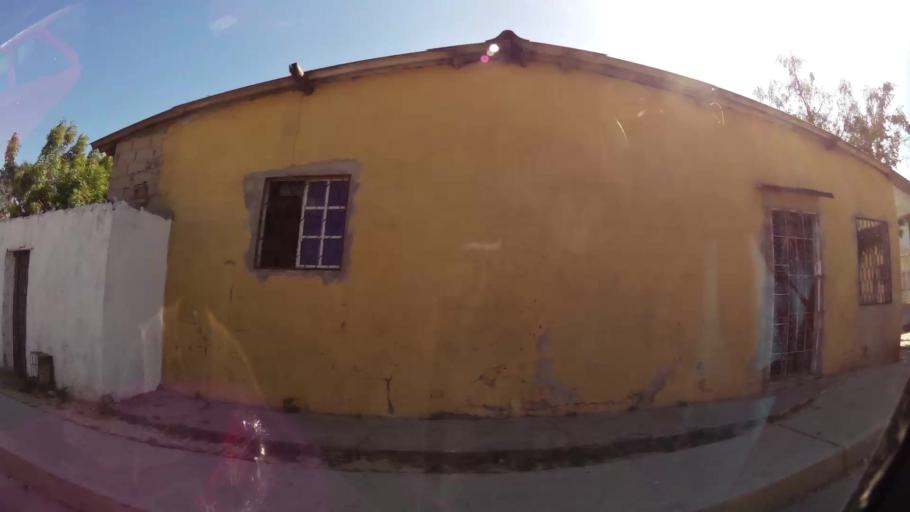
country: CO
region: Atlantico
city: Barranquilla
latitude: 10.9312
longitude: -74.8104
